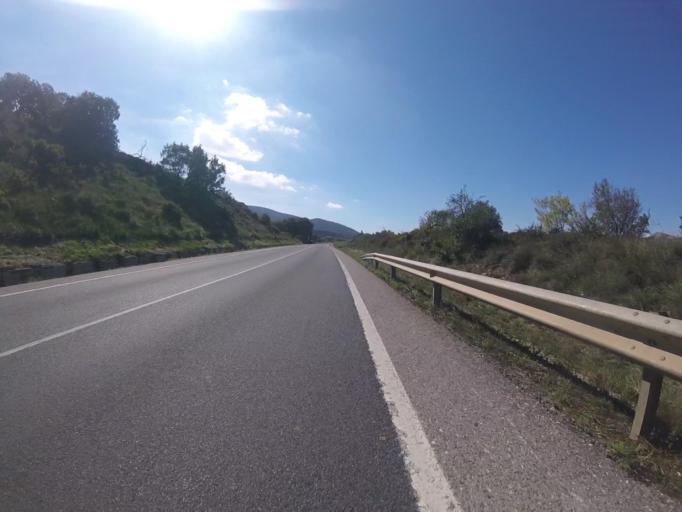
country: ES
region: Valencia
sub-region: Provincia de Castello
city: Sarratella
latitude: 40.3308
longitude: -0.0154
